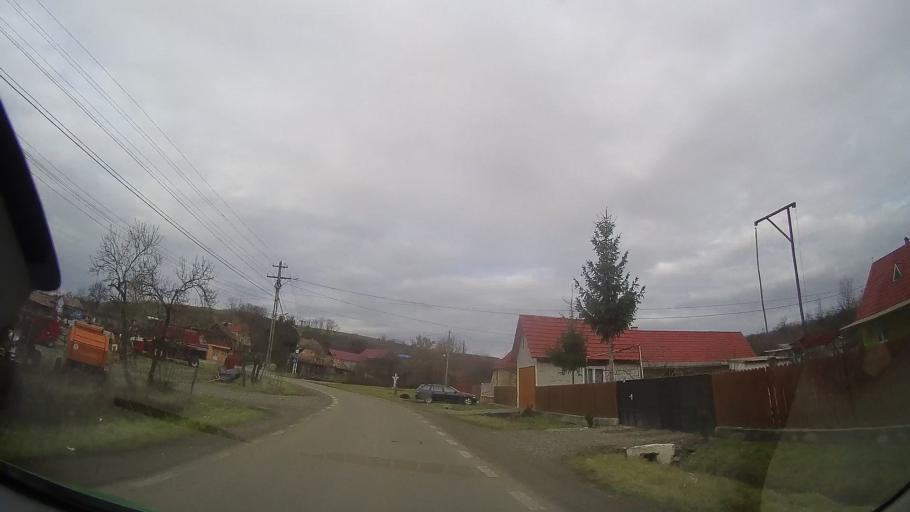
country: RO
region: Mures
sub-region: Comuna Cozma
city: Cozma
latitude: 46.8118
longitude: 24.5120
